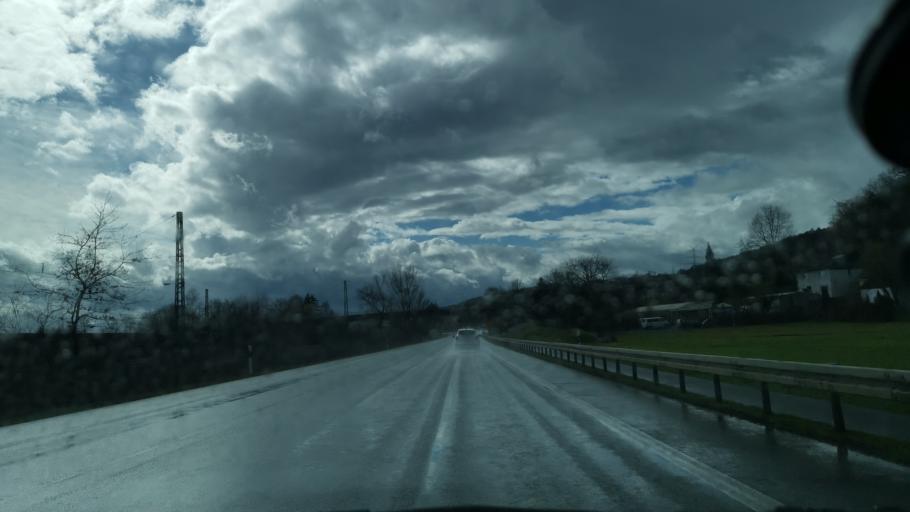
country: DE
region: Hesse
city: Breitenbach
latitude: 50.9249
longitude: 9.7626
